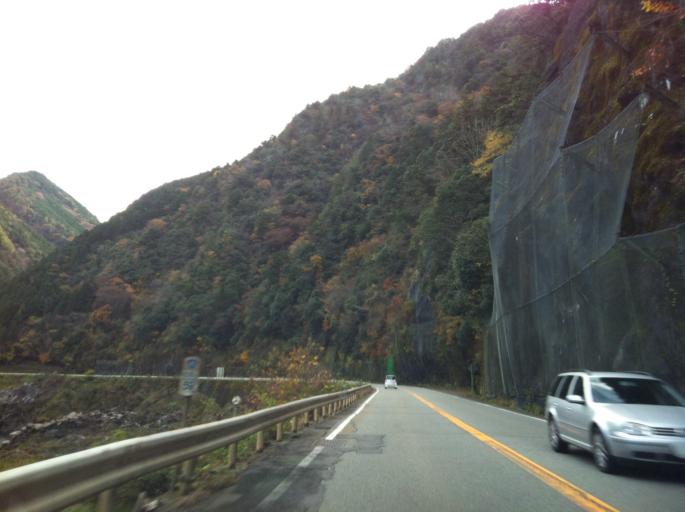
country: JP
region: Gifu
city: Mitake
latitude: 35.5510
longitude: 137.1814
